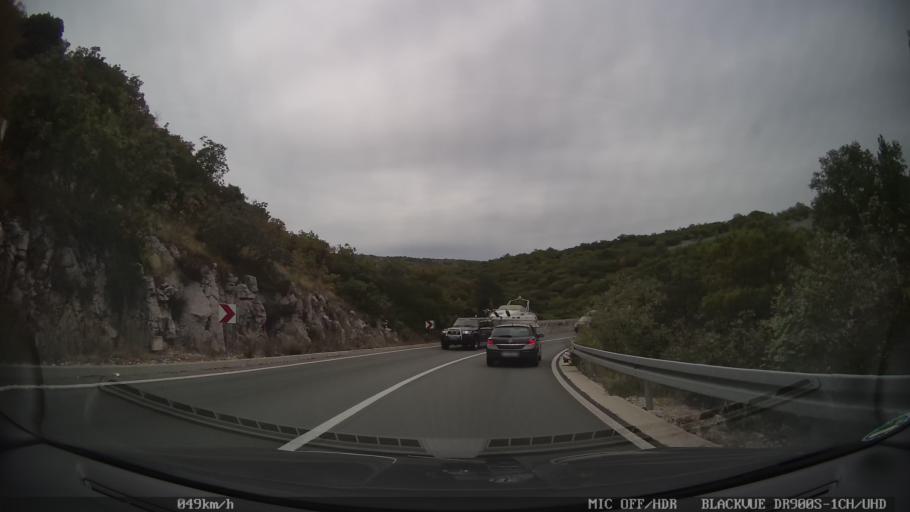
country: HR
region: Primorsko-Goranska
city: Novi Vinodolski
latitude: 45.1212
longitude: 14.8065
